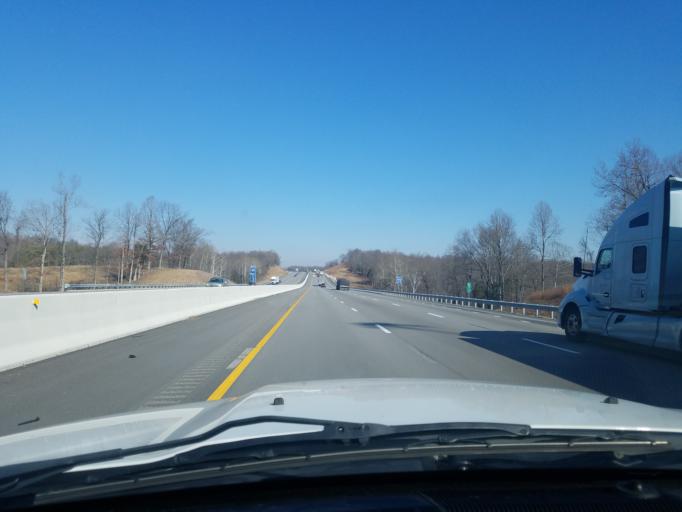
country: US
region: Kentucky
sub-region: Hart County
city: Munfordville
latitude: 37.3873
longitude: -85.8857
